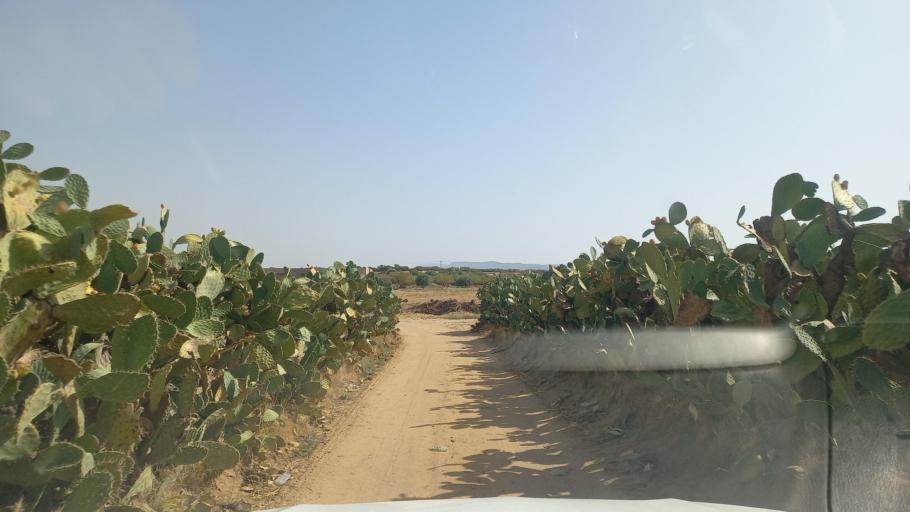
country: TN
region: Al Qasrayn
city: Kasserine
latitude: 35.2511
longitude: 9.0435
